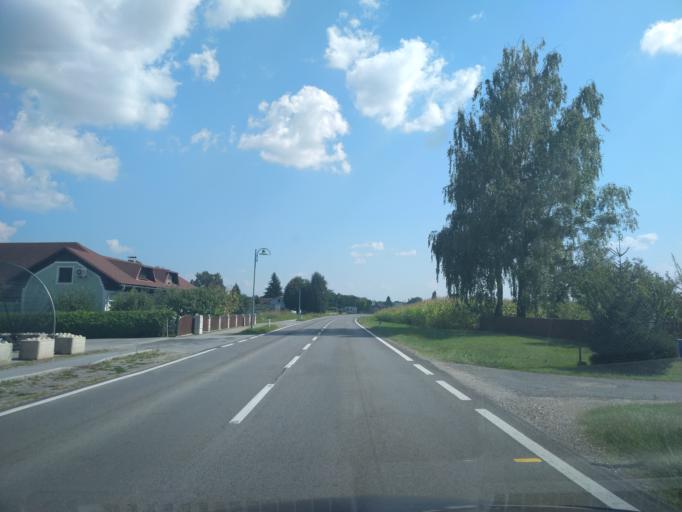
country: AT
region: Styria
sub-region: Politischer Bezirk Leibnitz
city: Gabersdorf
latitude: 46.7872
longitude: 15.5627
